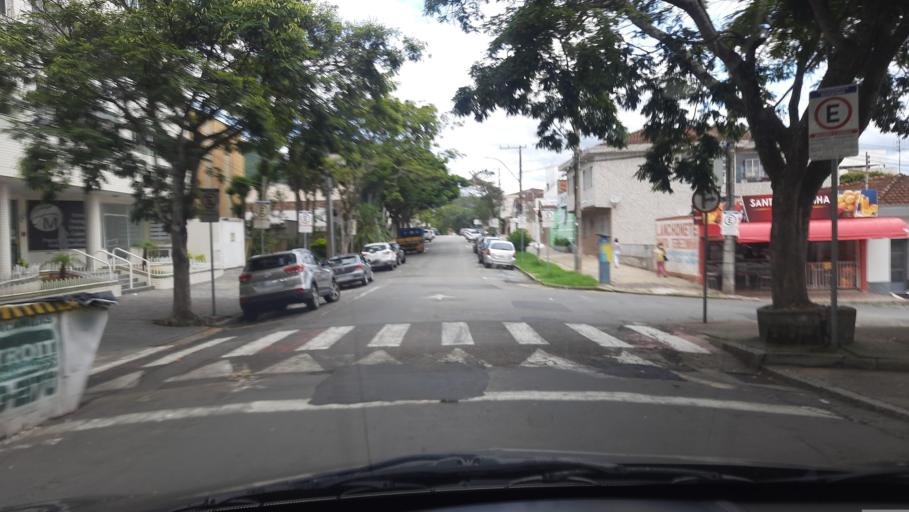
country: BR
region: Minas Gerais
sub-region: Pocos De Caldas
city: Pocos de Caldas
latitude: -21.7802
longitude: -46.5663
